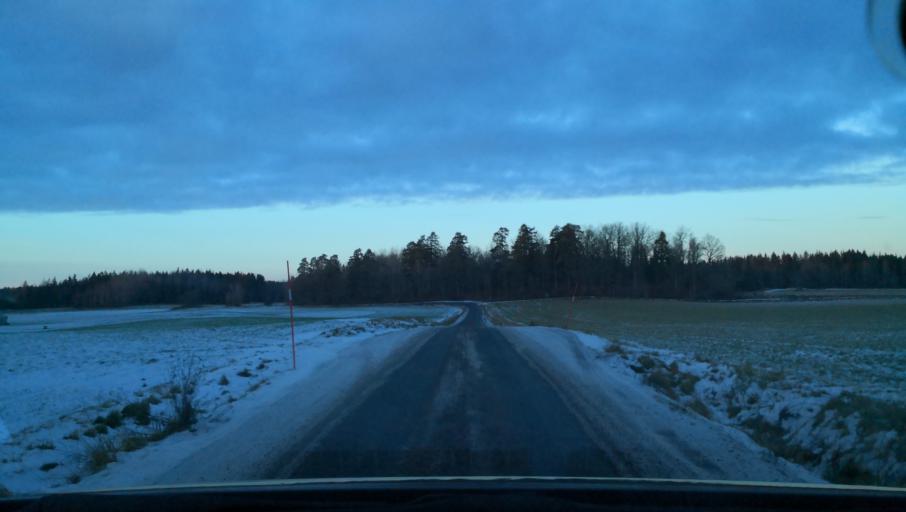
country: SE
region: Soedermanland
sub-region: Eskilstuna Kommun
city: Skogstorp
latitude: 59.2298
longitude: 16.3354
